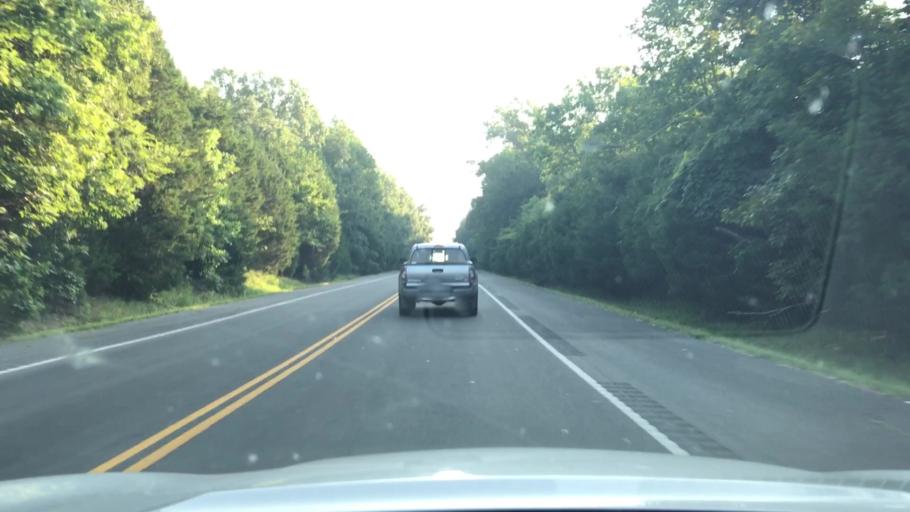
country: US
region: Tennessee
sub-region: Rutherford County
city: La Vergne
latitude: 36.0887
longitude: -86.5619
